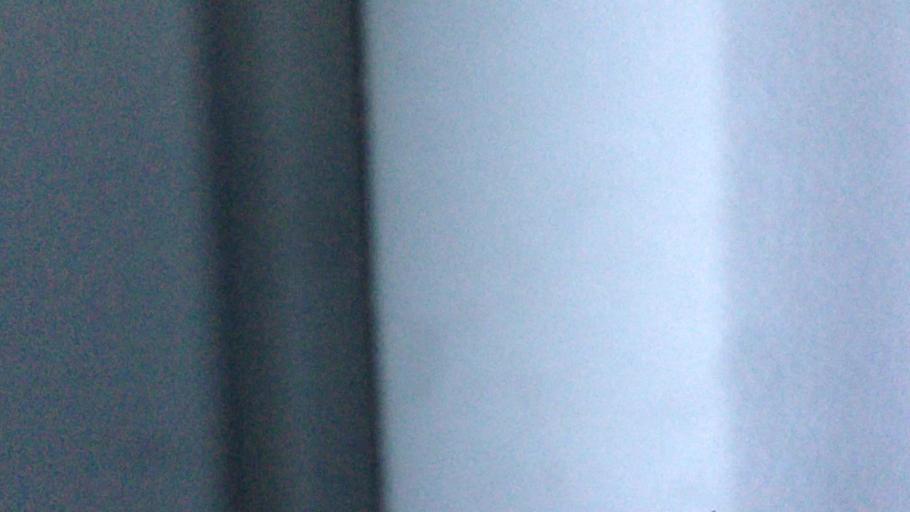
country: US
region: New York
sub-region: Dutchess County
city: Rhinebeck
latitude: 41.9527
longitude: -73.9184
